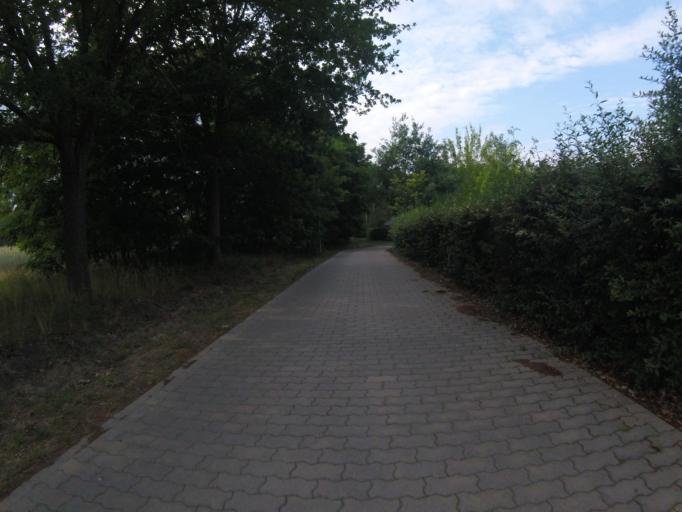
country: DE
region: Brandenburg
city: Bestensee
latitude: 52.2500
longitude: 13.6241
